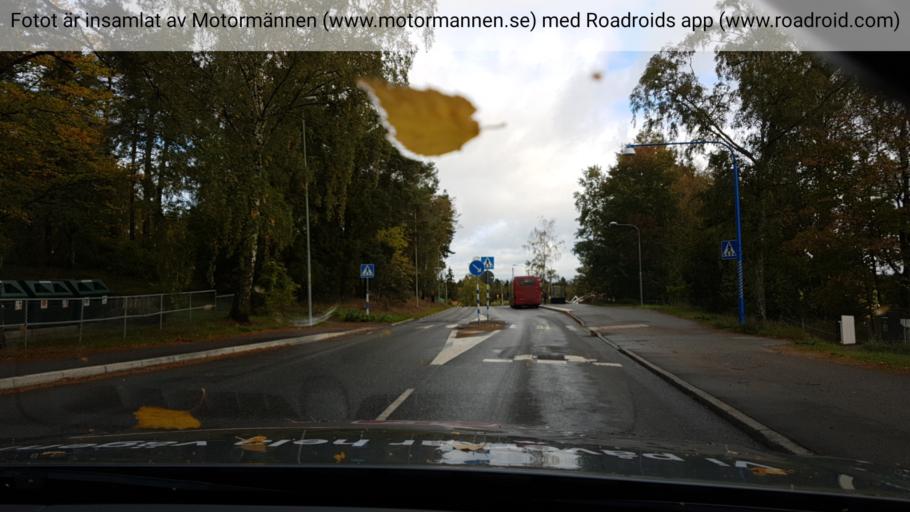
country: SE
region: Stockholm
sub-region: Haninge Kommun
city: Haninge
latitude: 59.1852
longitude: 18.1826
